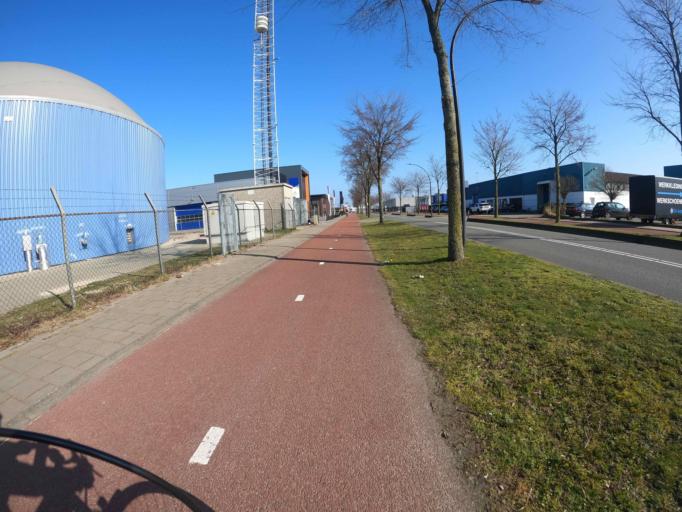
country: NL
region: Gelderland
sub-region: Gemeente Harderwijk
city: Harderwijk
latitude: 52.3575
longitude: 5.6349
